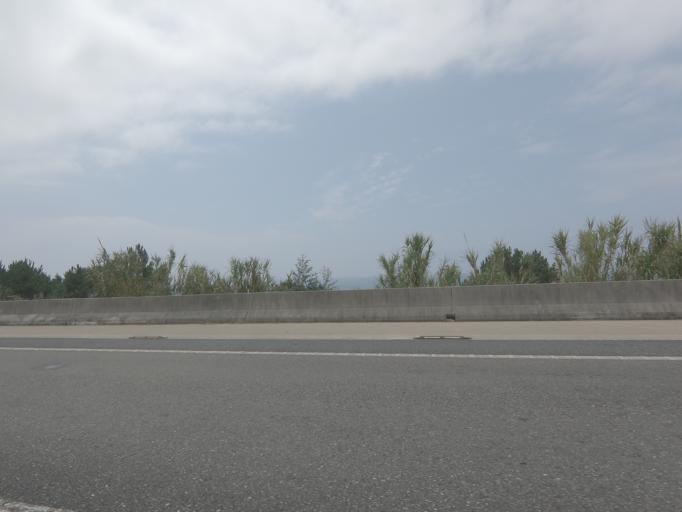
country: ES
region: Galicia
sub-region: Provincia de Pontevedra
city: Oia
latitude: 41.9704
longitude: -8.8840
